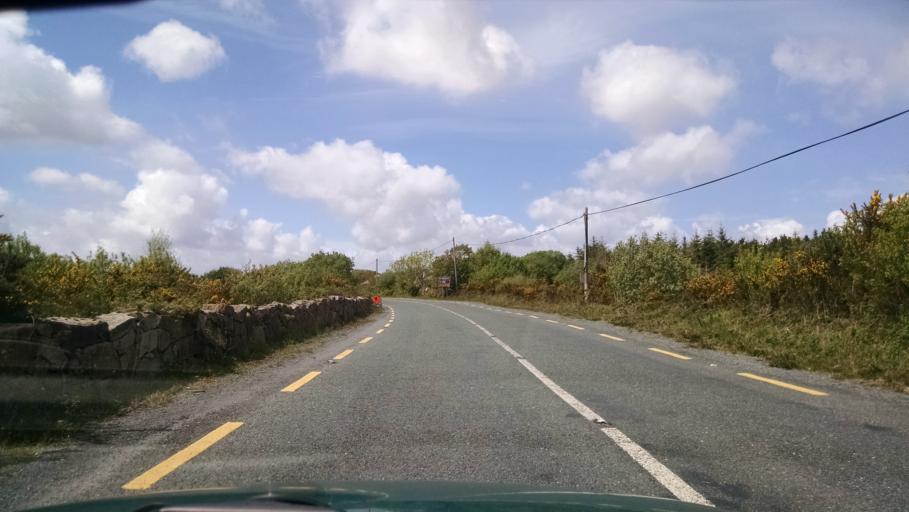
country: IE
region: Connaught
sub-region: County Galway
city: Oughterard
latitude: 53.3880
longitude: -9.6145
